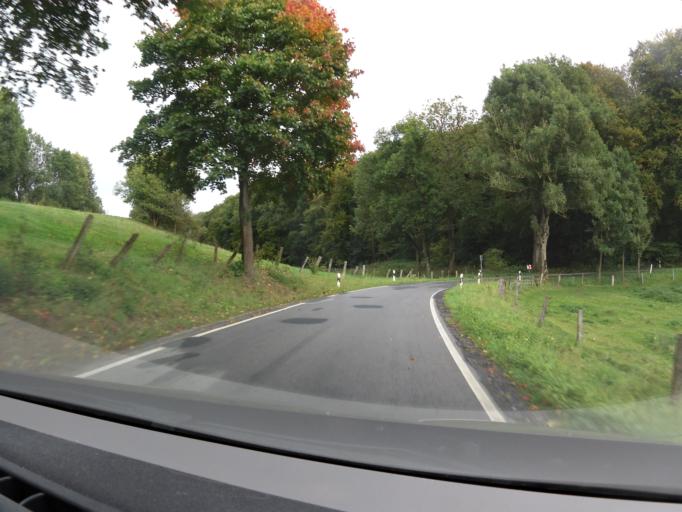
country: DE
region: Lower Saxony
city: Derental
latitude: 51.6983
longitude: 9.4465
